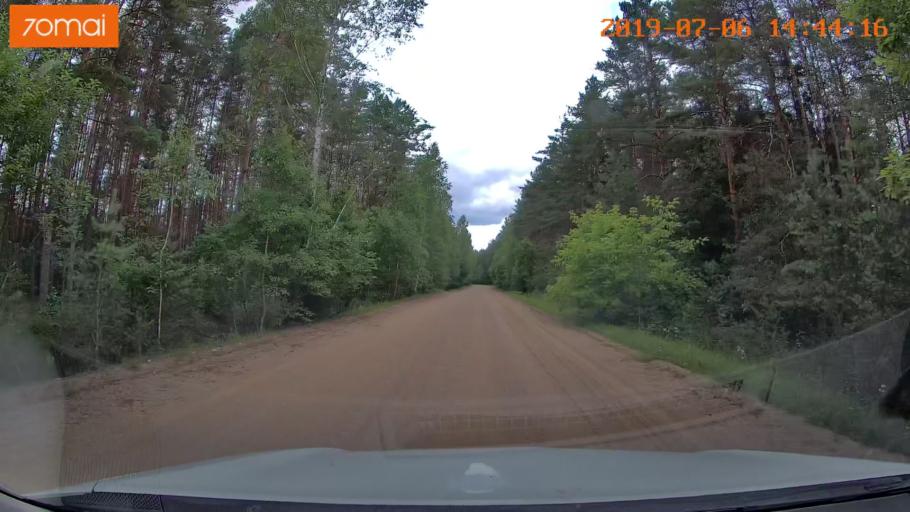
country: BY
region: Minsk
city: Ivyanyets
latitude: 53.9600
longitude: 26.6948
